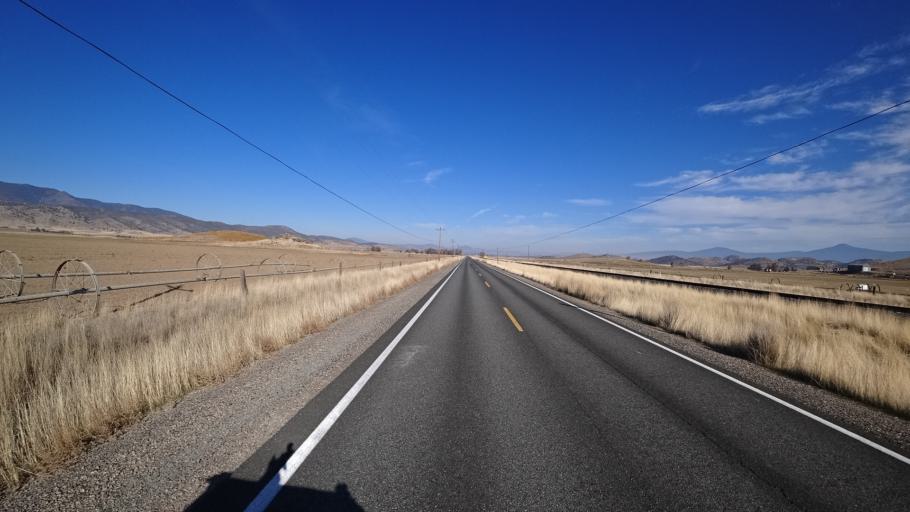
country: US
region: California
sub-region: Siskiyou County
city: Montague
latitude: 41.5585
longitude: -122.5259
